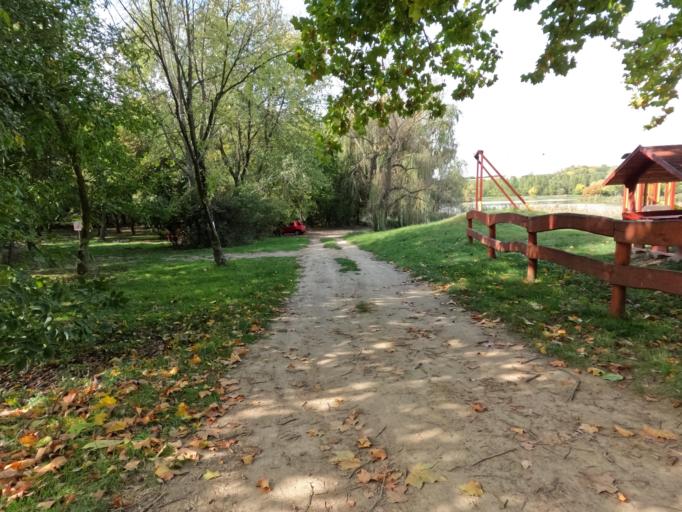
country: HU
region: Tolna
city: Szentgalpuszta
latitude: 46.3555
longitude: 18.6185
